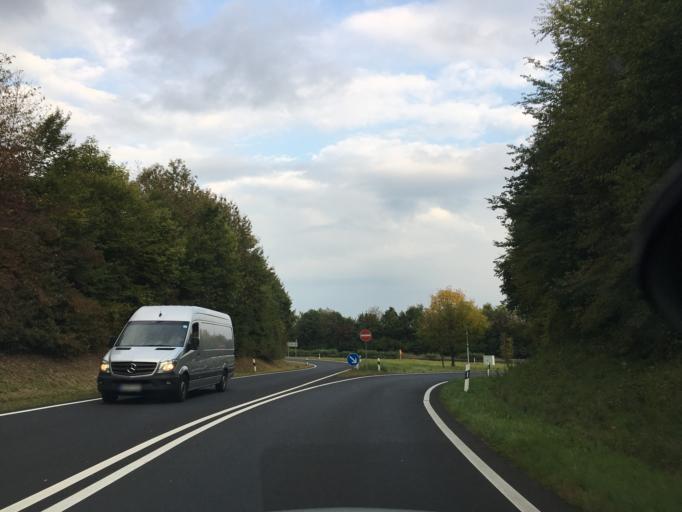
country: DE
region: Hesse
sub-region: Regierungsbezirk Darmstadt
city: Steinau an der Strasse
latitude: 50.3200
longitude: 9.4345
